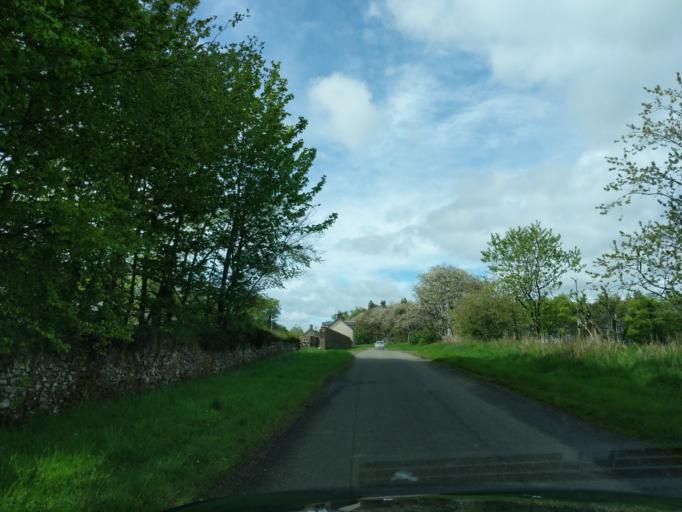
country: GB
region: Scotland
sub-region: The Scottish Borders
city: Saint Boswells
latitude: 55.6463
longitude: -2.5659
